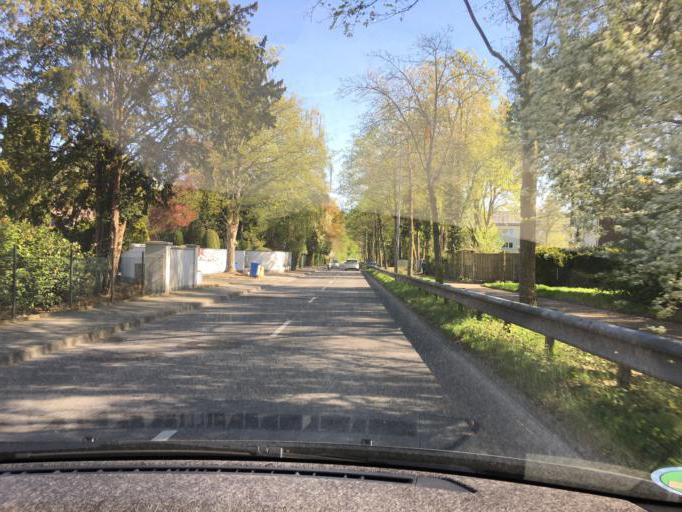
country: DE
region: North Rhine-Westphalia
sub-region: Regierungsbezirk Dusseldorf
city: Monchengladbach
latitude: 51.1367
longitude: 6.4066
